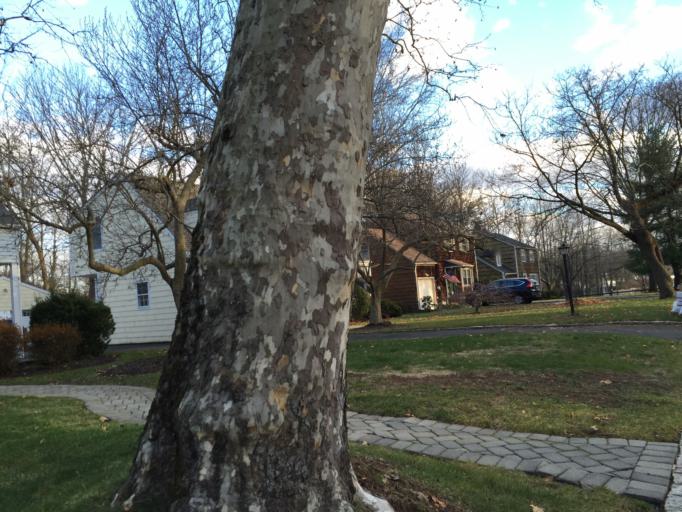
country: US
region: New Jersey
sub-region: Union County
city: New Providence
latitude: 40.7046
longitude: -74.4114
